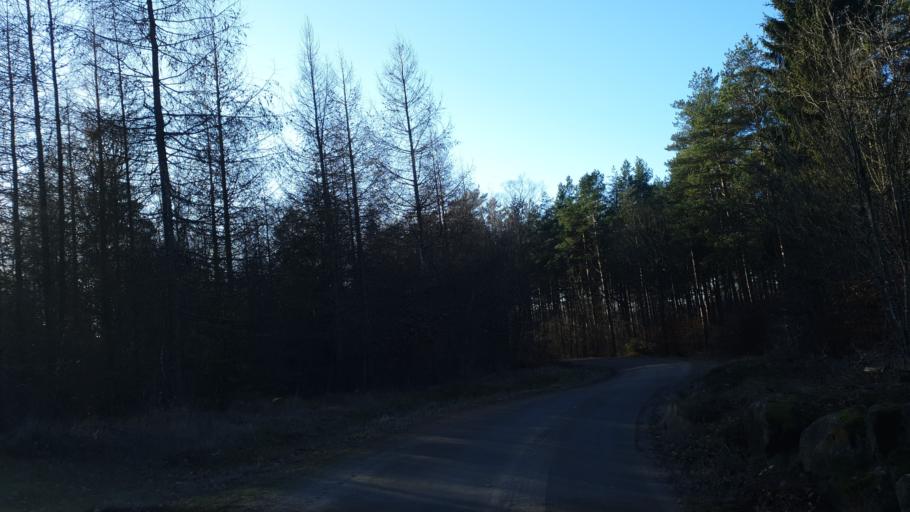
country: SE
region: Blekinge
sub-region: Karlskrona Kommun
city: Nattraby
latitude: 56.2567
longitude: 15.4102
